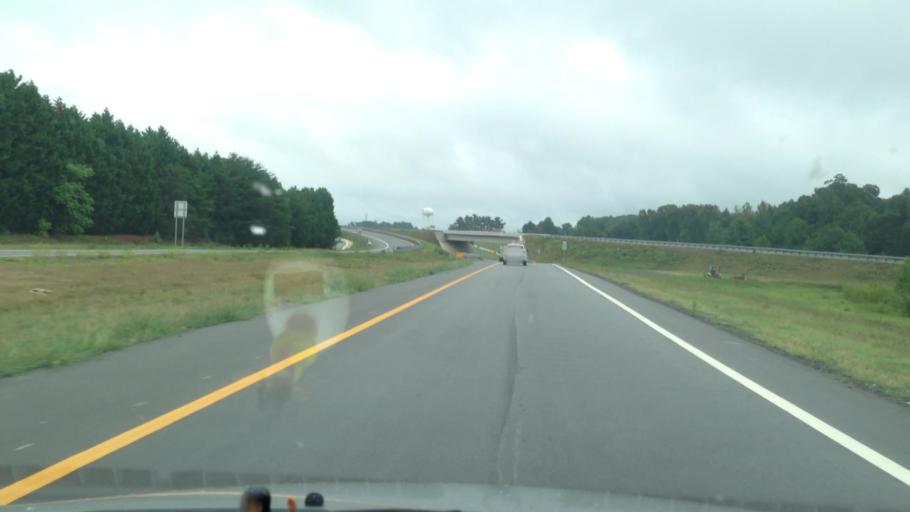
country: US
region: North Carolina
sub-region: Guilford County
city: Stokesdale
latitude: 36.2817
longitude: -79.9405
